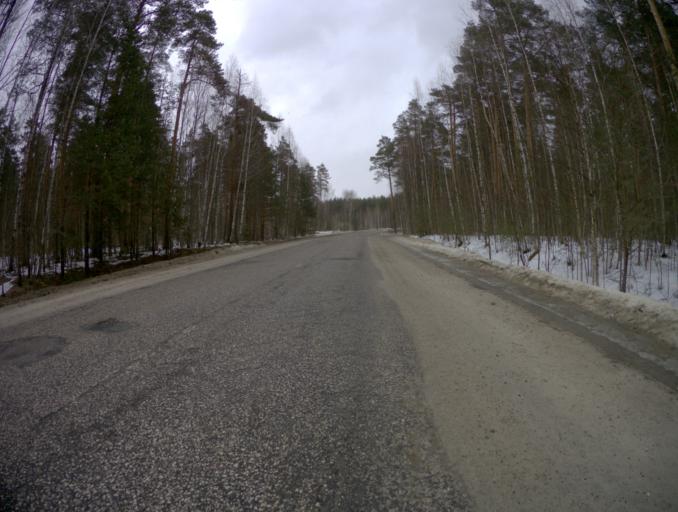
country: RU
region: Vladimir
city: Bogolyubovo
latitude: 56.1545
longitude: 40.5411
